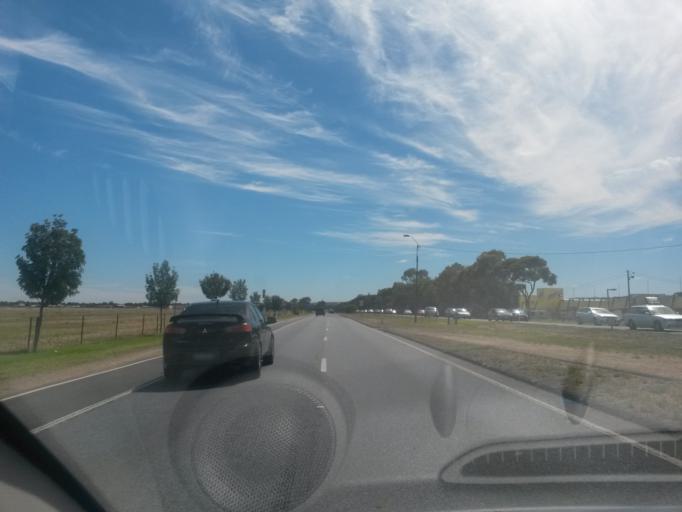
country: AU
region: South Australia
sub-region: Salisbury
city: Ingle Farm
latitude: -34.8005
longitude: 138.6391
